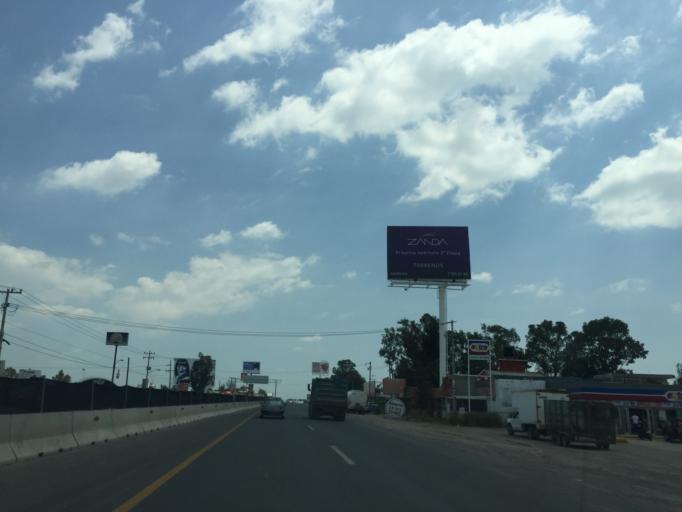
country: MX
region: Guanajuato
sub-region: Leon
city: Fraccionamiento Paseo de las Torres
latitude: 21.1850
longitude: -101.7448
